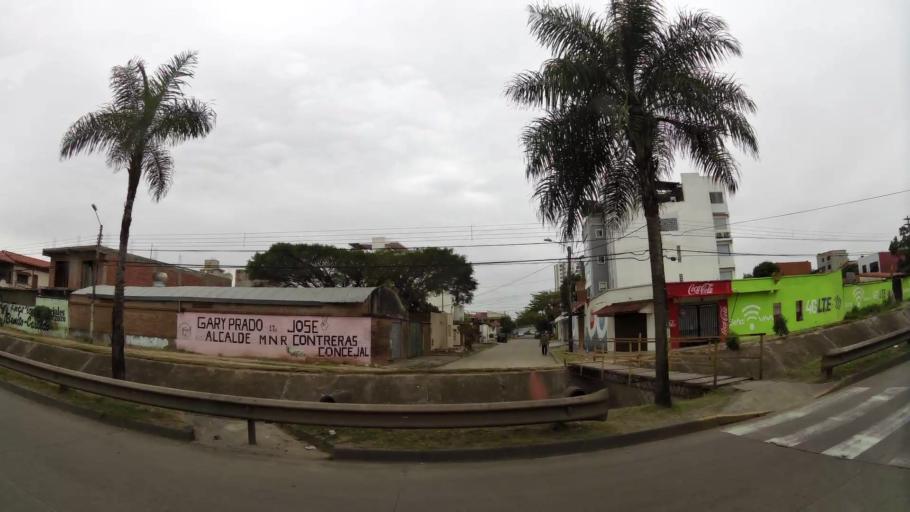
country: BO
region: Santa Cruz
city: Santa Cruz de la Sierra
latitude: -17.7705
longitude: -63.2038
